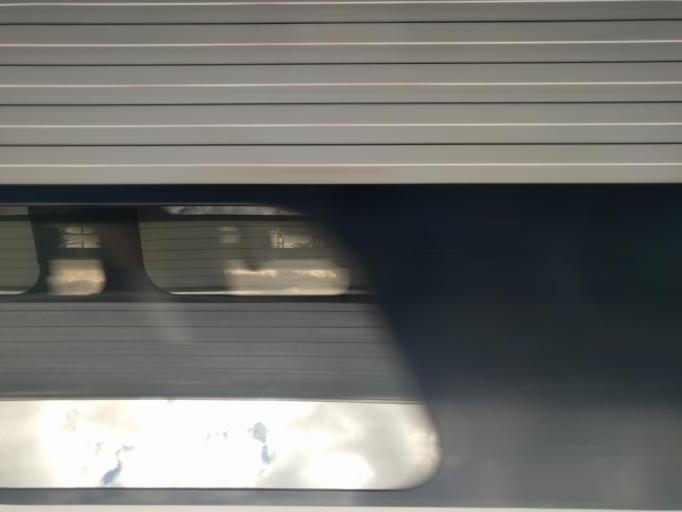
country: DK
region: Zealand
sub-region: Slagelse Kommune
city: Slagelse
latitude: 55.4075
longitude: 11.3469
